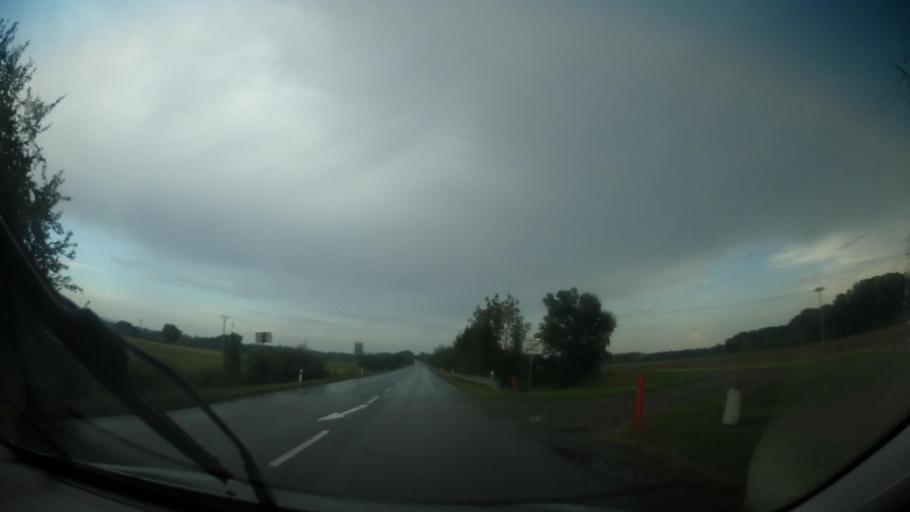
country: CZ
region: Olomoucky
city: Cervenka
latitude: 49.7130
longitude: 17.1106
